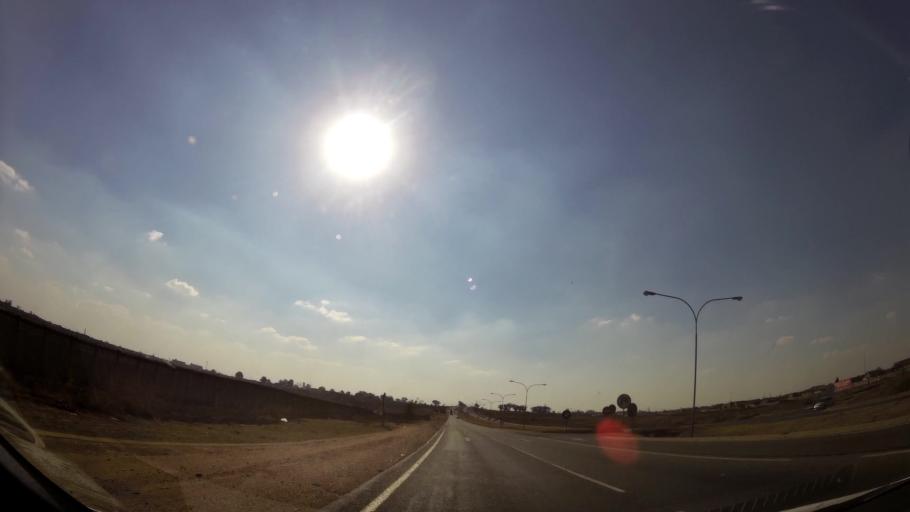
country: ZA
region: Gauteng
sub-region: Ekurhuleni Metropolitan Municipality
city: Benoni
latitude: -26.2288
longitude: 28.3214
